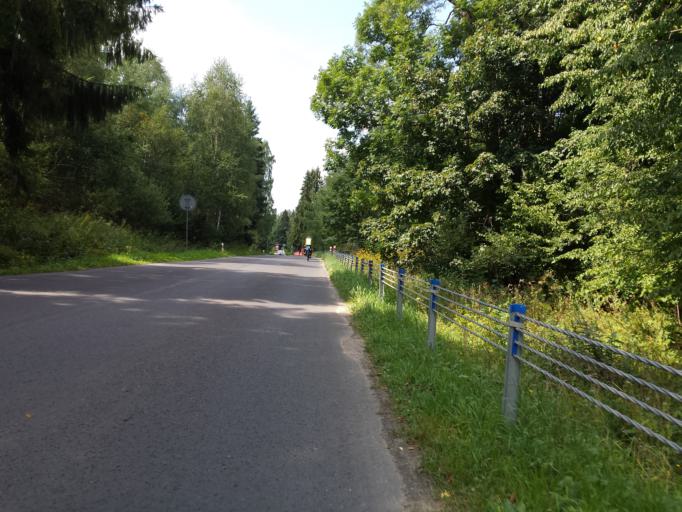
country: PL
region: Subcarpathian Voivodeship
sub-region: Powiat leski
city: Cisna
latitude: 49.1886
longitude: 22.3837
